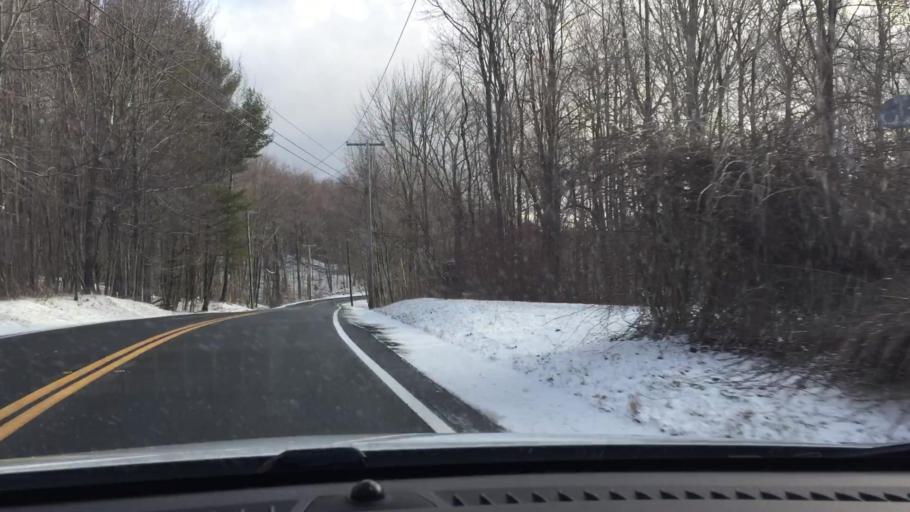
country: US
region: Massachusetts
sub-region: Berkshire County
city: Hinsdale
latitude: 42.4086
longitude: -73.1220
